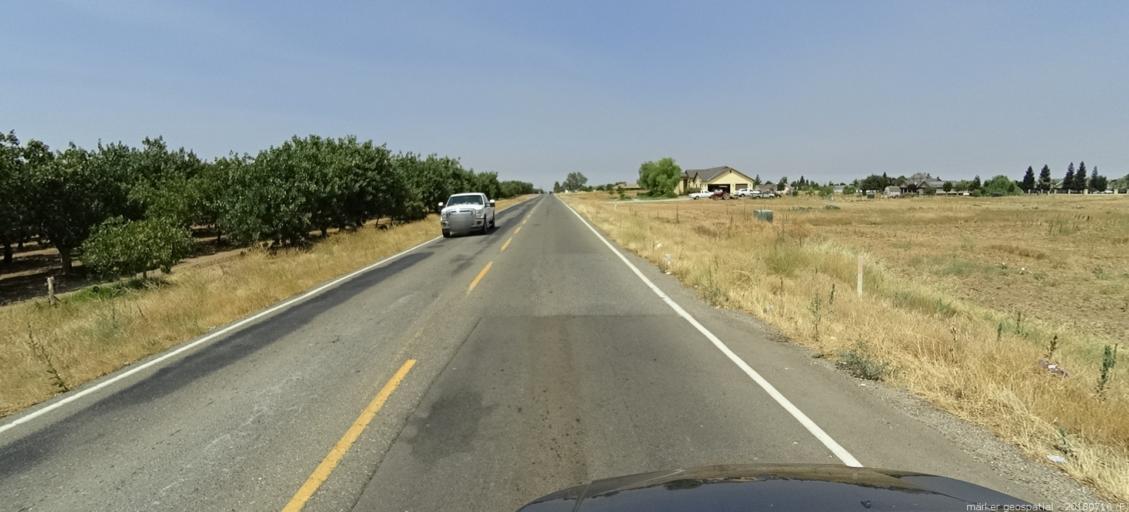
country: US
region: California
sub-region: Madera County
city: Madera Acres
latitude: 37.0542
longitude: -120.0205
